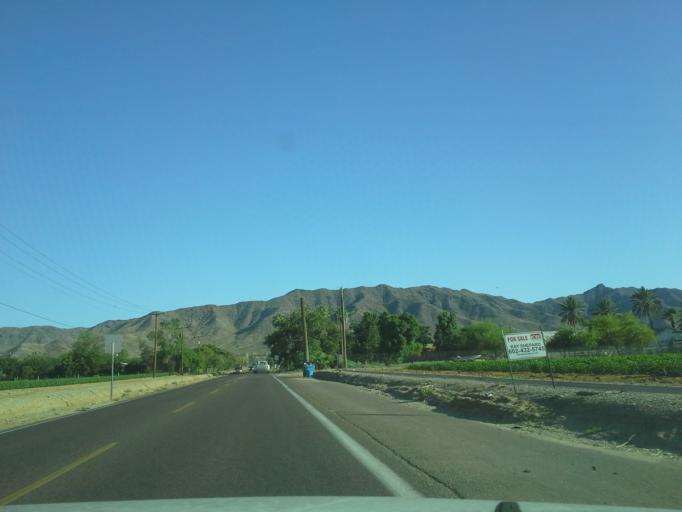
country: US
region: Arizona
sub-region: Maricopa County
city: Laveen
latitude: 33.3683
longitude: -112.1005
